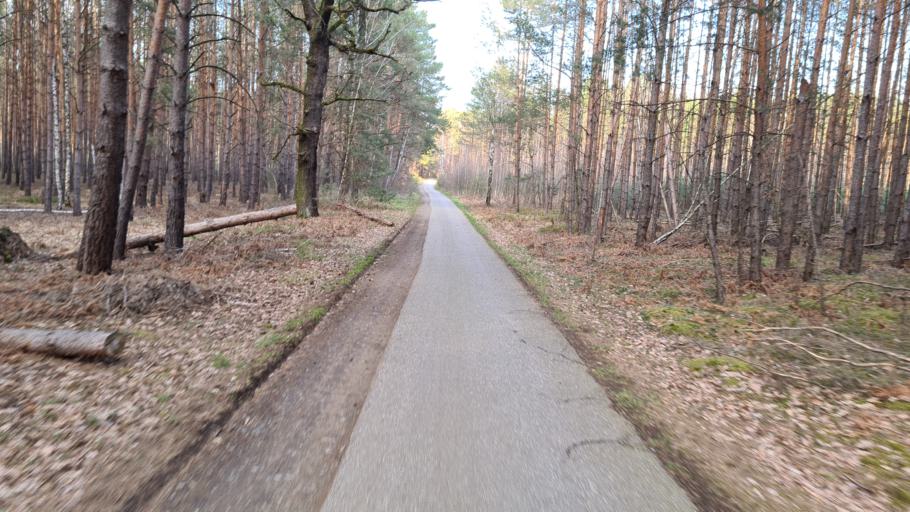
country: DE
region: Brandenburg
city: Schonborn
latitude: 51.5532
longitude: 13.5049
